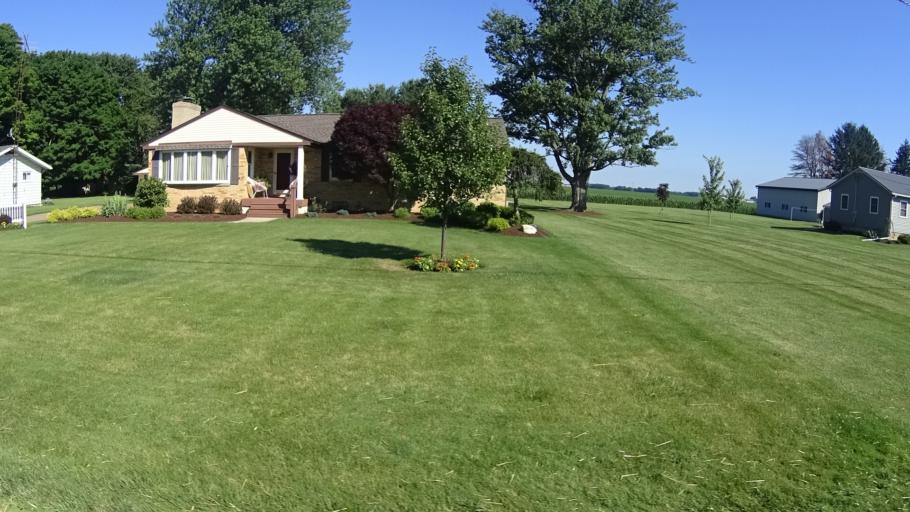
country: US
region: Ohio
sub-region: Erie County
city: Huron
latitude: 41.3609
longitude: -82.5983
